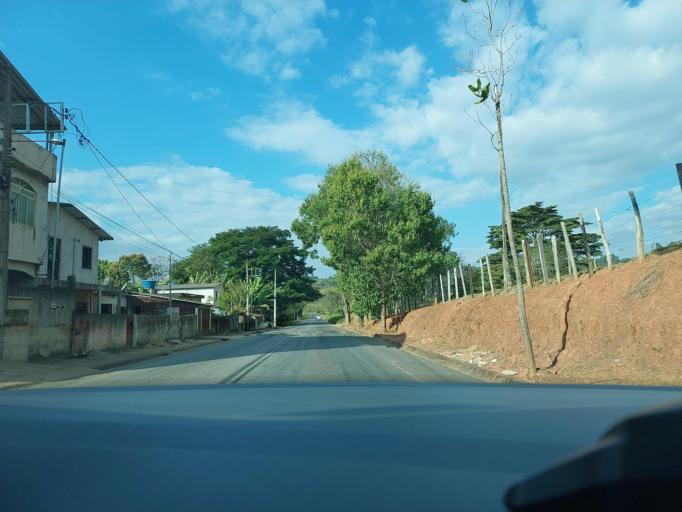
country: BR
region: Minas Gerais
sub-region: Vicosa
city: Vicosa
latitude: -20.8325
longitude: -42.7919
